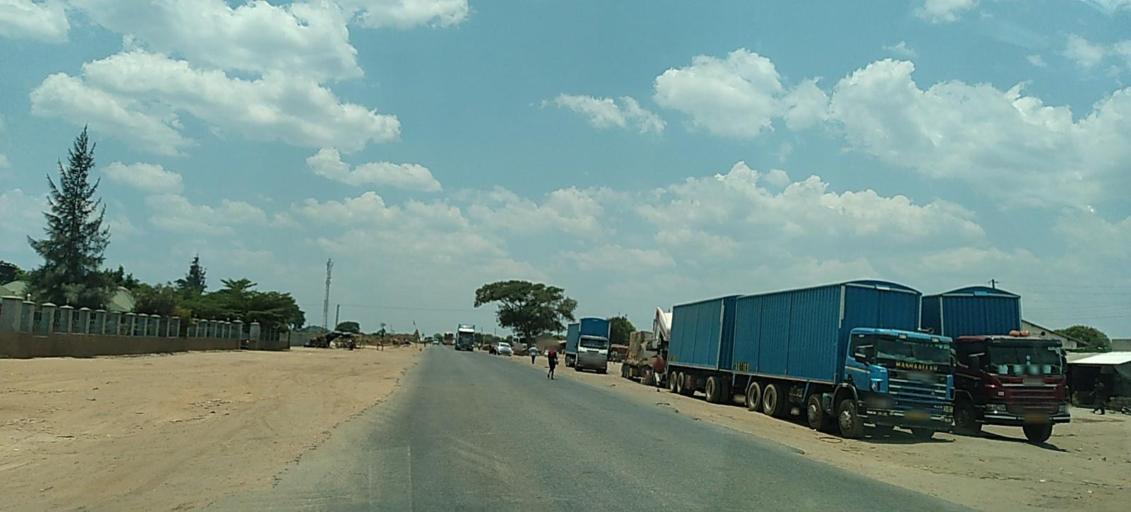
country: ZM
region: Central
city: Kapiri Mposhi
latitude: -13.8927
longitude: 28.6554
